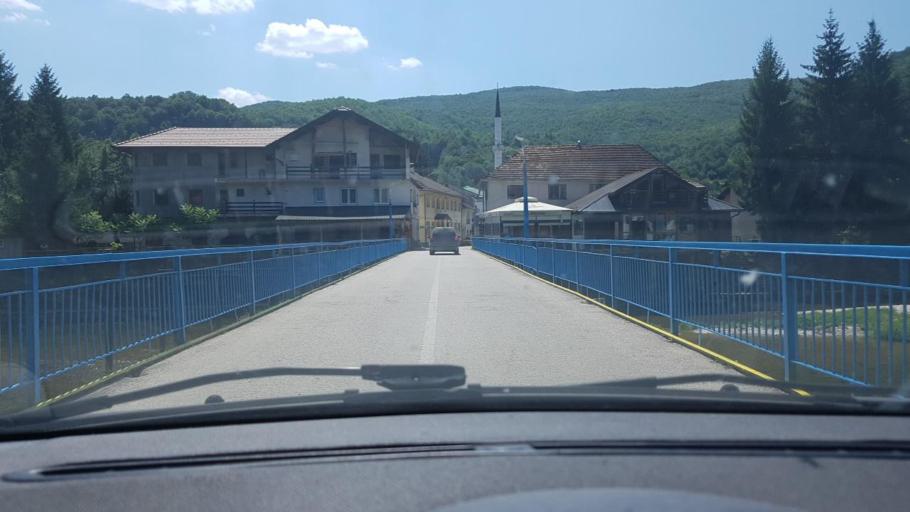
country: BA
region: Federation of Bosnia and Herzegovina
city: Orasac
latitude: 44.5627
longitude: 16.0891
